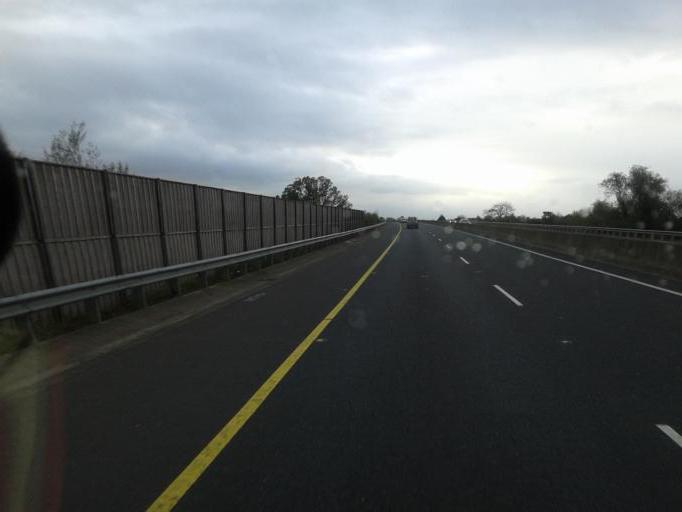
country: IE
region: Munster
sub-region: County Limerick
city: Castleconnell
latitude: 52.7097
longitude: -8.4803
